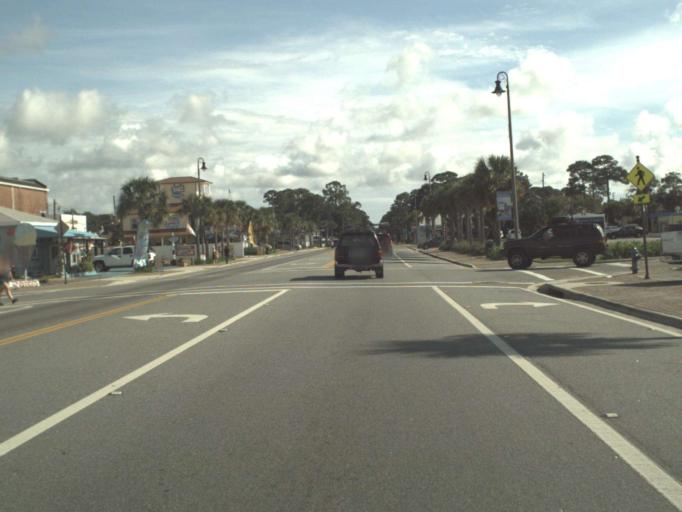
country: US
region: Florida
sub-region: Gulf County
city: Port Saint Joe
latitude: 29.8143
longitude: -85.3044
